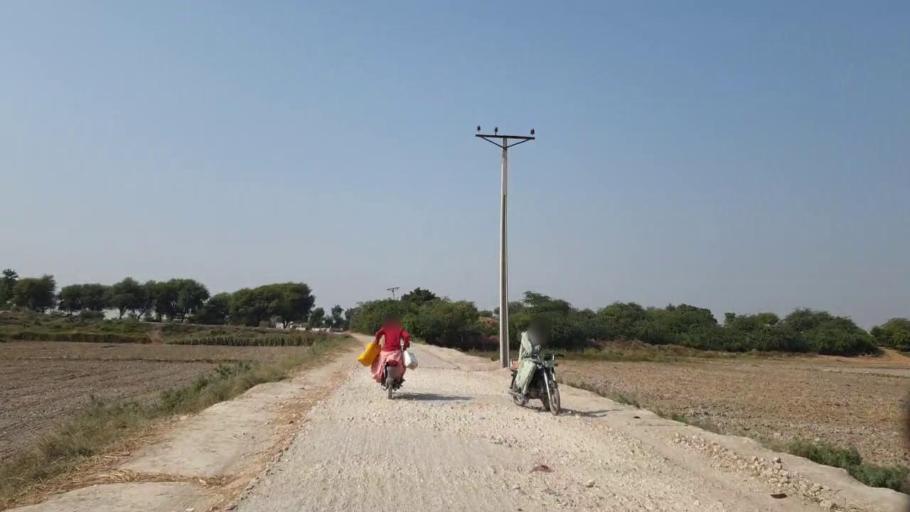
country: PK
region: Sindh
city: Bulri
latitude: 24.9597
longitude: 68.3301
